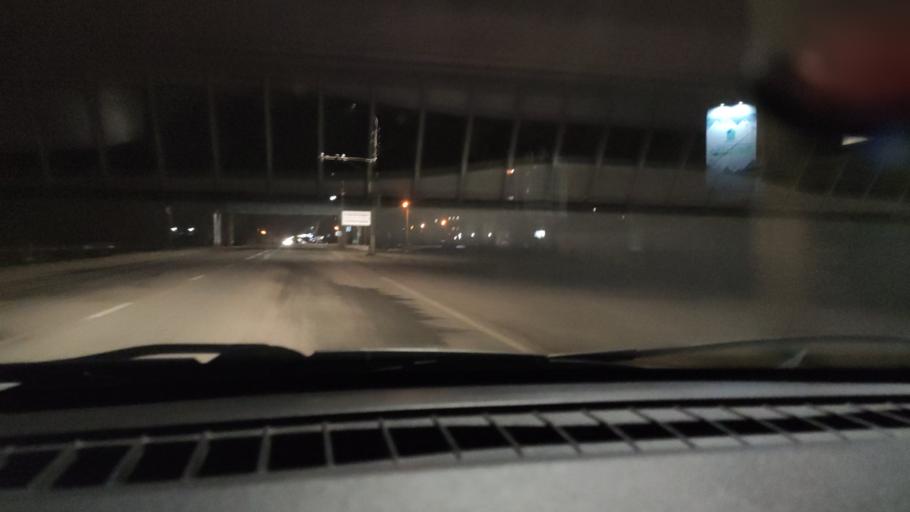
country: RU
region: Bashkortostan
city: Sterlitamak
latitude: 53.6421
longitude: 55.8970
